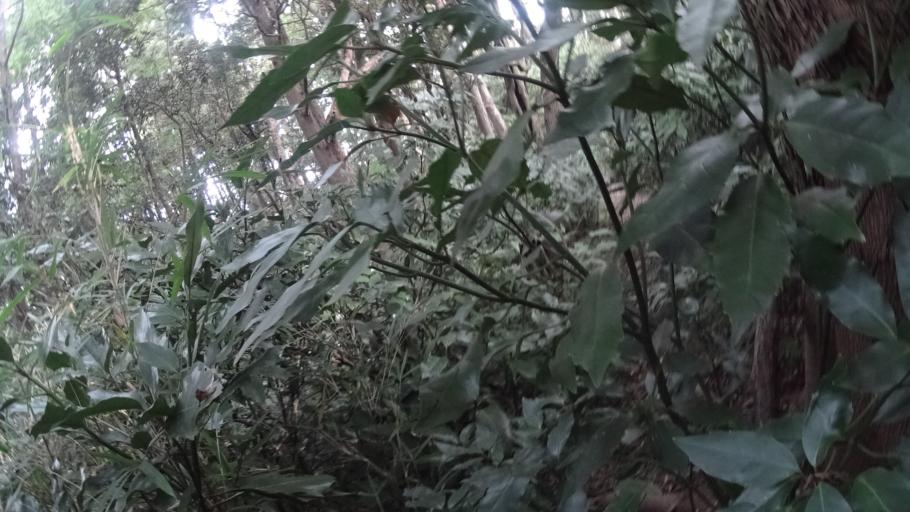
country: JP
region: Kanagawa
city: Zushi
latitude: 35.3559
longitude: 139.5973
